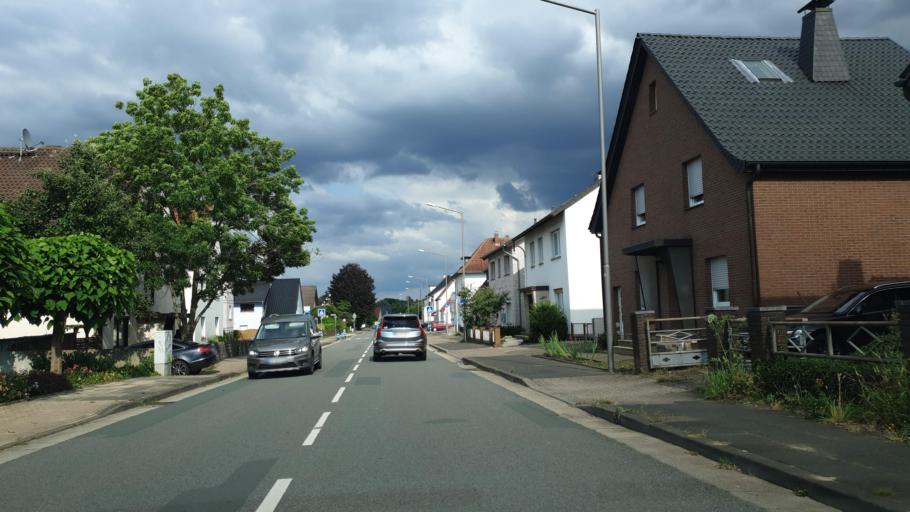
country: DE
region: North Rhine-Westphalia
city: Bad Oeynhausen
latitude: 52.2023
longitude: 8.7711
